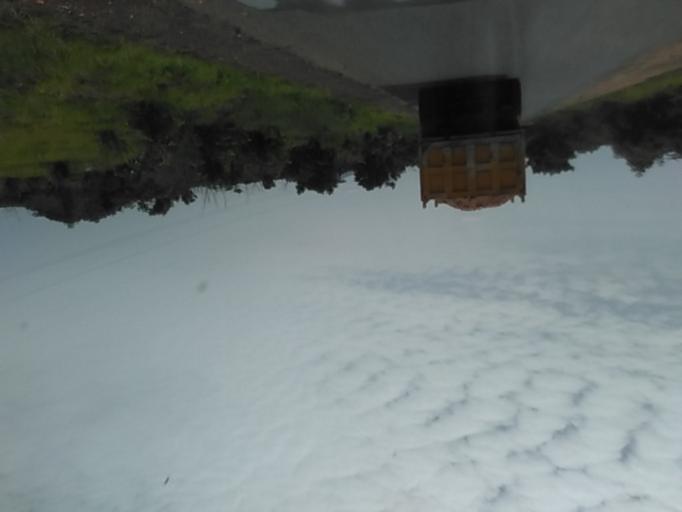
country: GH
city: Akropong
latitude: 6.0955
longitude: 0.0574
